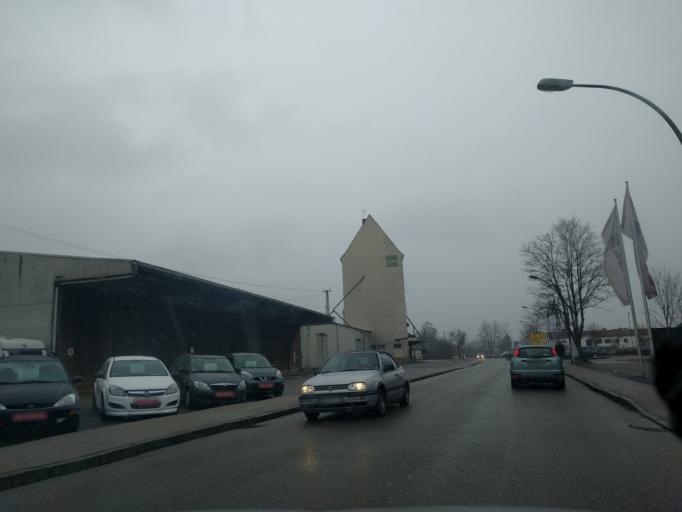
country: DE
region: Bavaria
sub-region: Swabia
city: Donauwoerth
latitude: 48.7170
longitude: 10.7653
